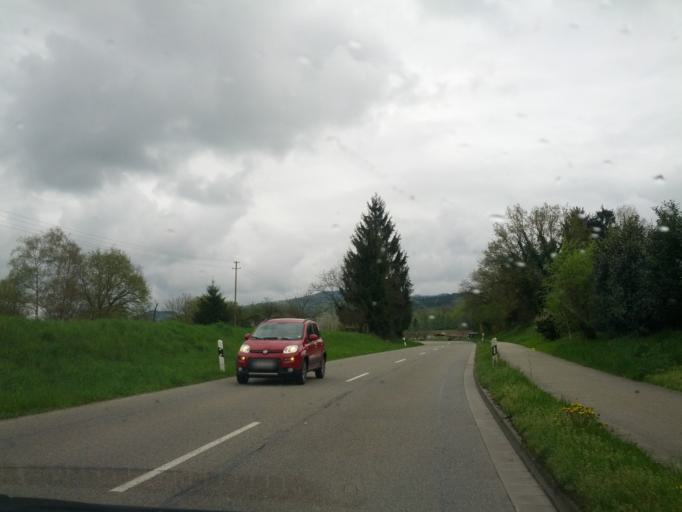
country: DE
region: Baden-Wuerttemberg
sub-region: Freiburg Region
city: Pfaffenweiler
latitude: 47.9130
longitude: 7.7588
